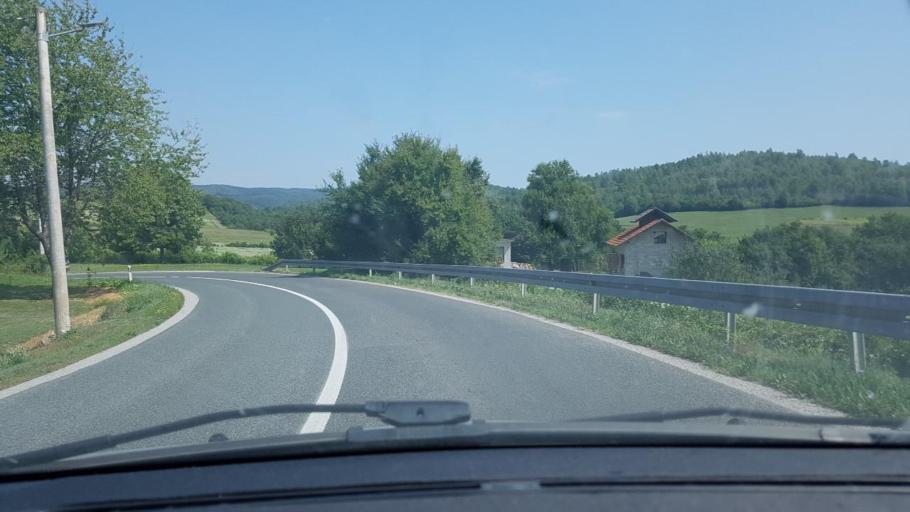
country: BA
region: Federation of Bosnia and Herzegovina
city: Velika Kladusa
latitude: 45.2088
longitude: 15.7716
